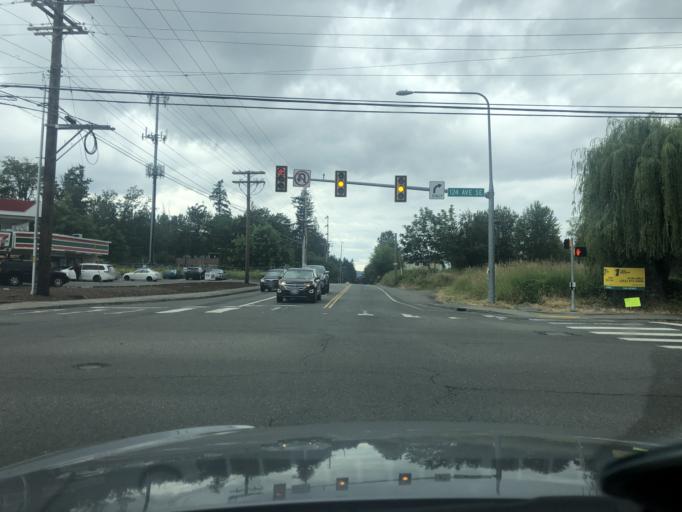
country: US
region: Washington
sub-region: King County
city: Lea Hill
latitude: 47.3225
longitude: -122.1763
